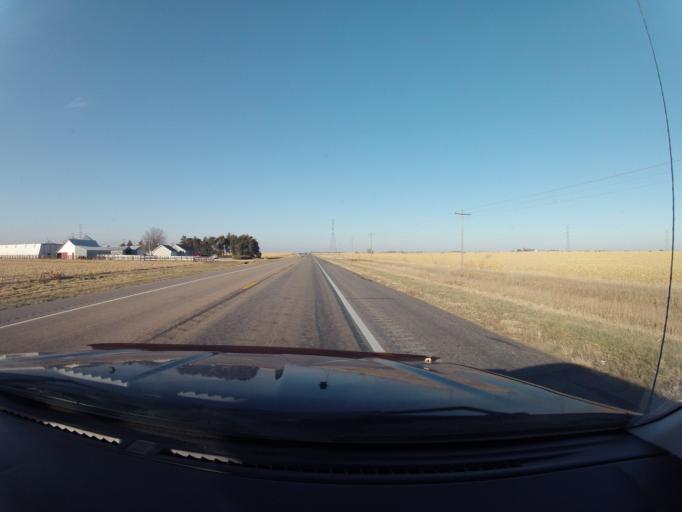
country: US
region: Nebraska
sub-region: Kearney County
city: Minden
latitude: 40.5418
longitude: -98.9518
